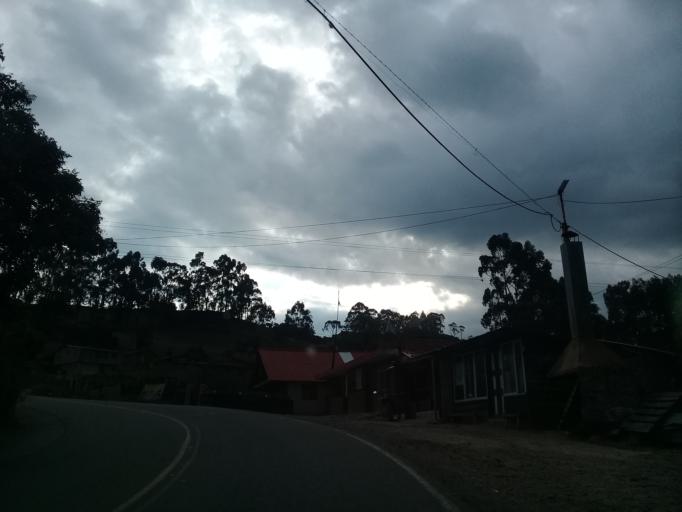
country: CO
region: Cundinamarca
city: Zipaquira
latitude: 5.0287
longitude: -74.0240
